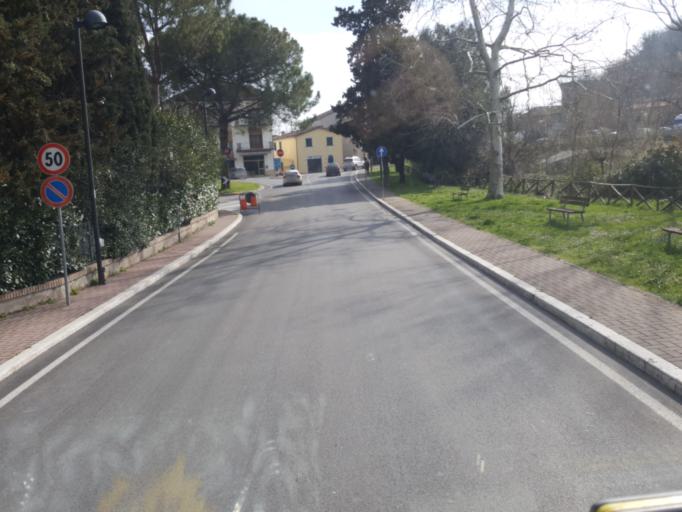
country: IT
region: The Marches
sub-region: Provincia di Macerata
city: Passo di Treia
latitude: 43.2834
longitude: 13.3320
